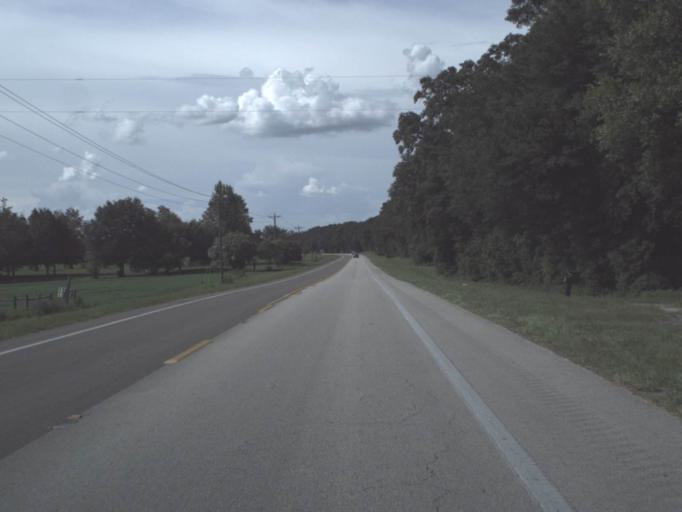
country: US
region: Florida
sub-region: Gilchrist County
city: Trenton
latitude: 29.7369
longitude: -82.8578
